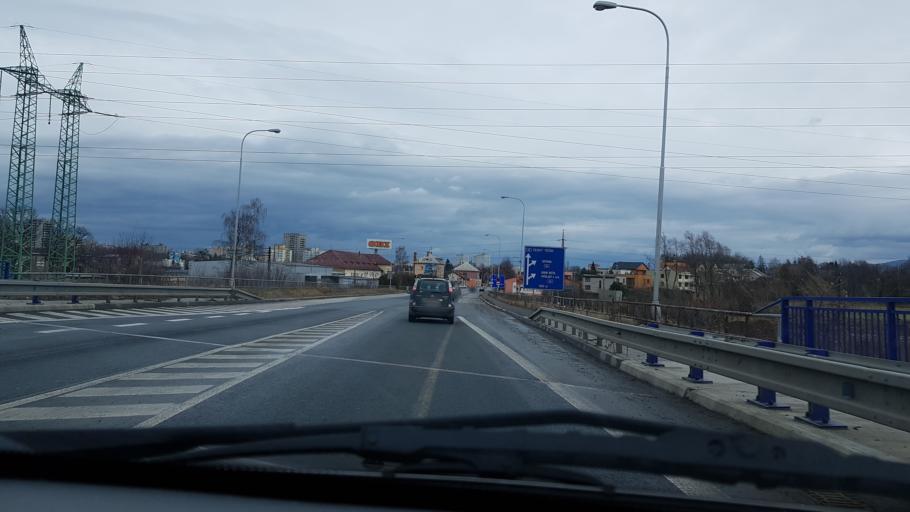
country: CZ
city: Sviadnov
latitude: 49.6700
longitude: 18.3218
